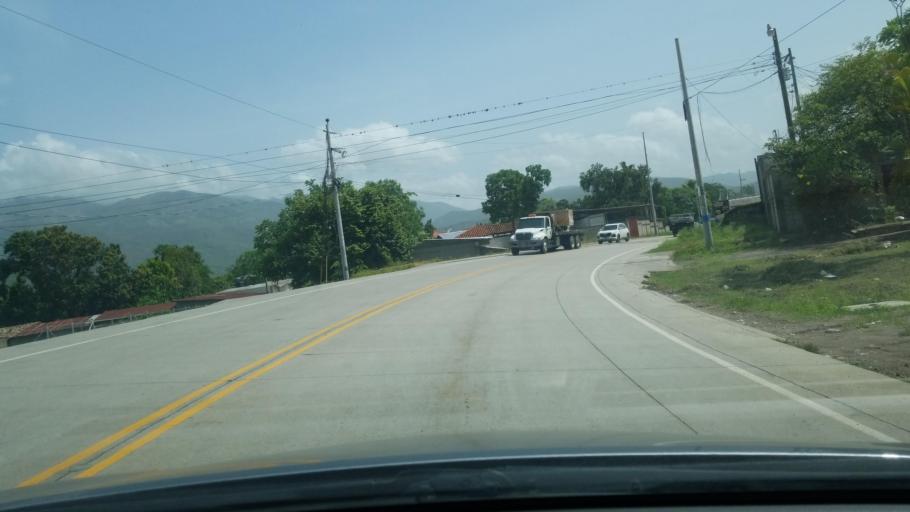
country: HN
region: Copan
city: Florida
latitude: 15.0240
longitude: -88.8324
